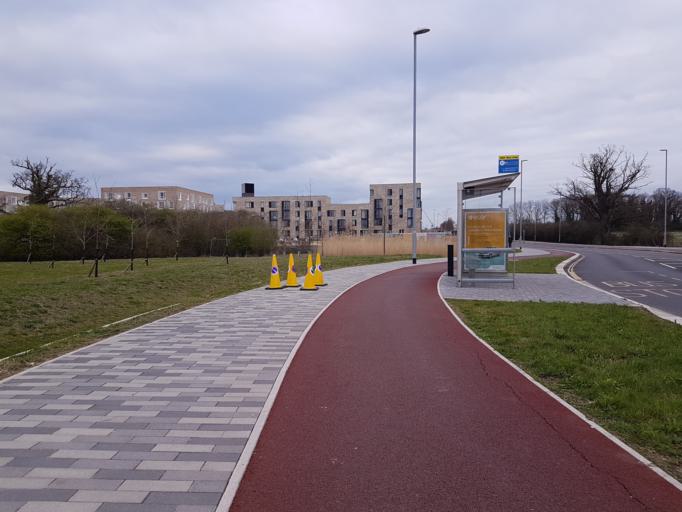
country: GB
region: England
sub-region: Cambridgeshire
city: Girton
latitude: 52.2153
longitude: 0.0862
